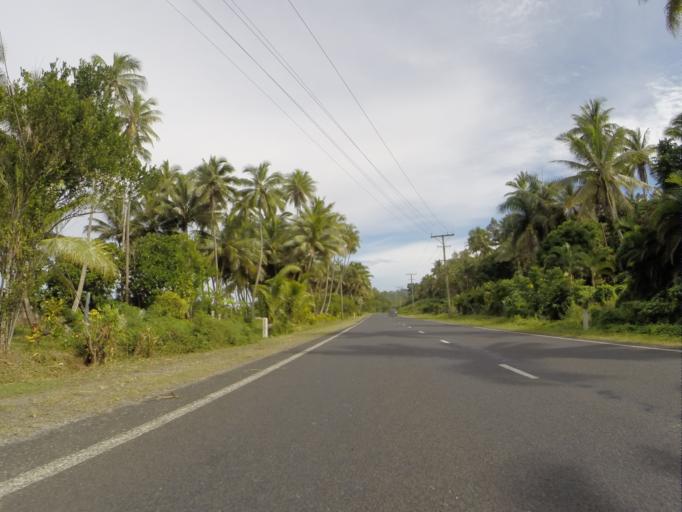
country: FJ
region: Western
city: Nadi
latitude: -18.2027
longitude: 177.6862
